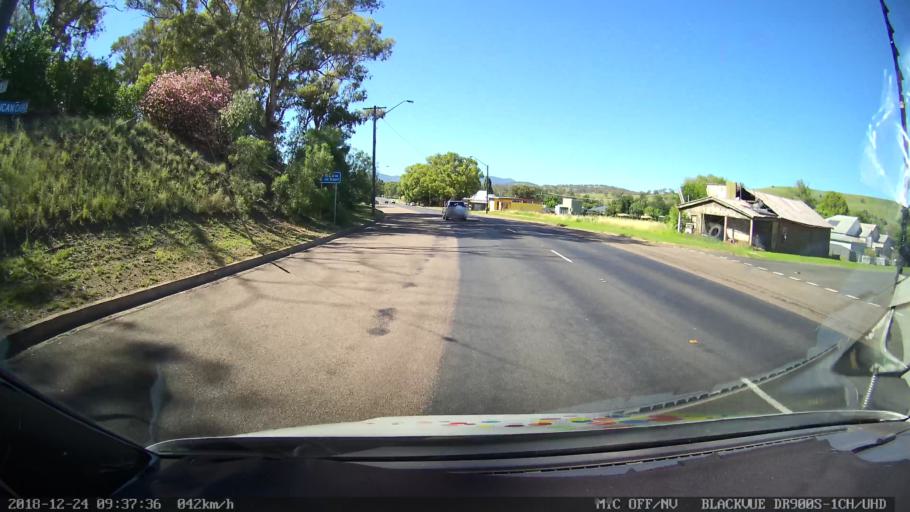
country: AU
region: New South Wales
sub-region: Liverpool Plains
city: Quirindi
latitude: -31.6463
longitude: 150.7258
